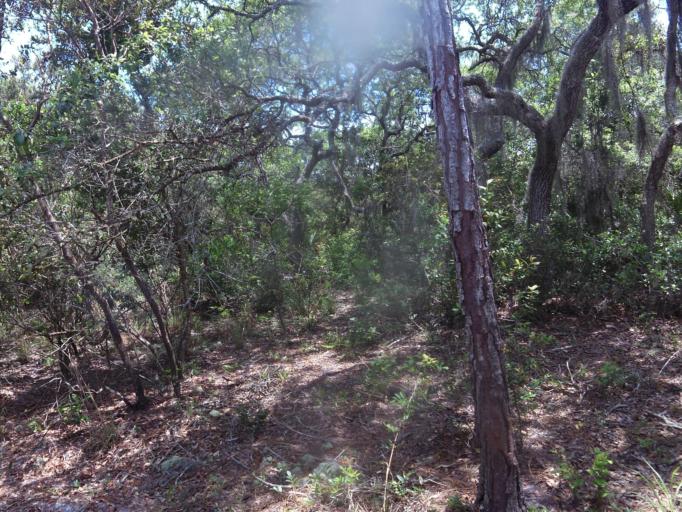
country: US
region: Florida
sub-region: Nassau County
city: Fernandina Beach
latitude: 30.4960
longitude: -81.4915
